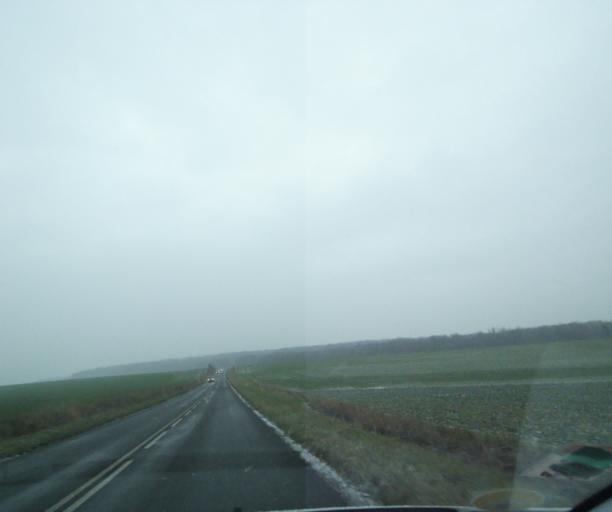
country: FR
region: Champagne-Ardenne
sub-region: Departement de la Haute-Marne
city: Wassy
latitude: 48.4797
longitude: 5.0044
